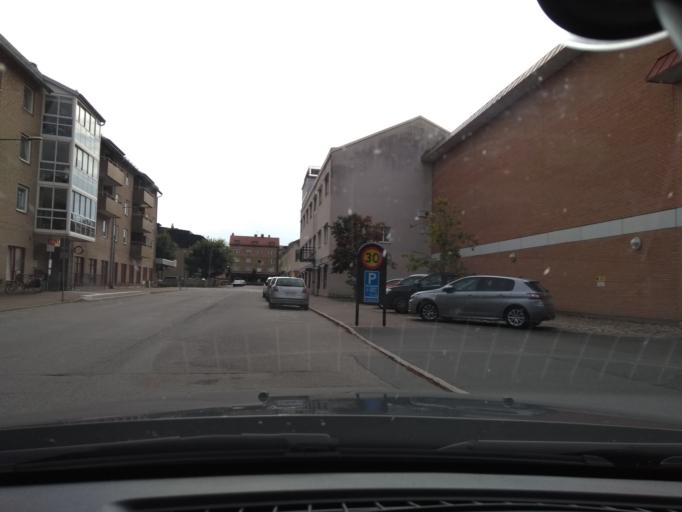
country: SE
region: Joenkoeping
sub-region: Nassjo Kommun
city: Nassjo
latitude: 57.6527
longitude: 14.6997
